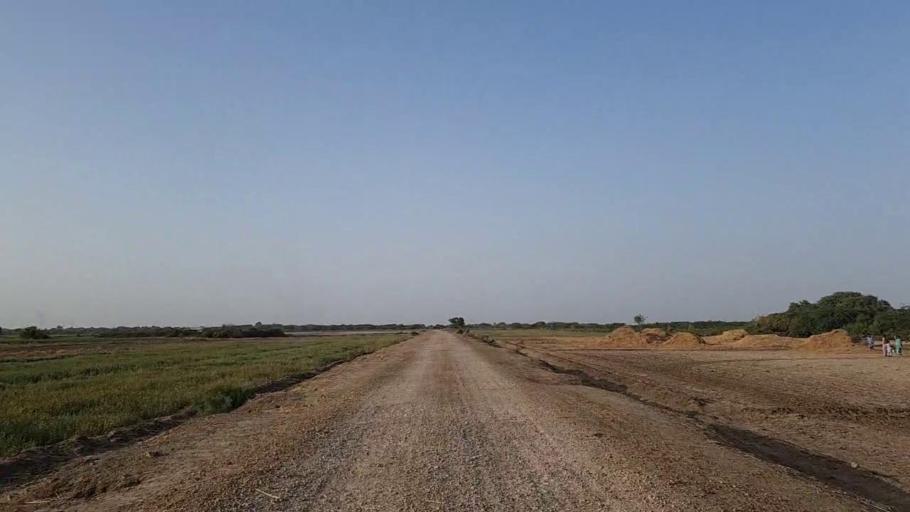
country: PK
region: Sindh
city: Jati
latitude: 24.3786
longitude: 68.1480
